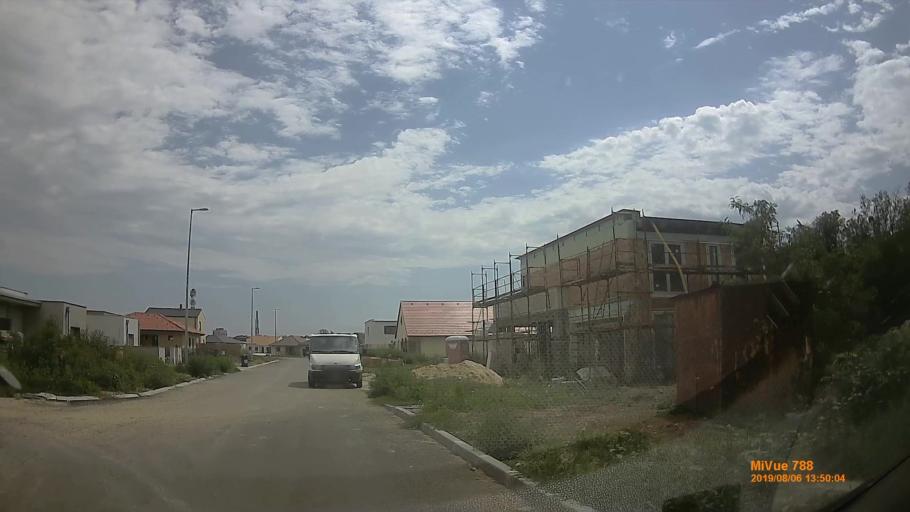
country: HU
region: Vas
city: Szombathely
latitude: 47.2518
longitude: 16.5983
